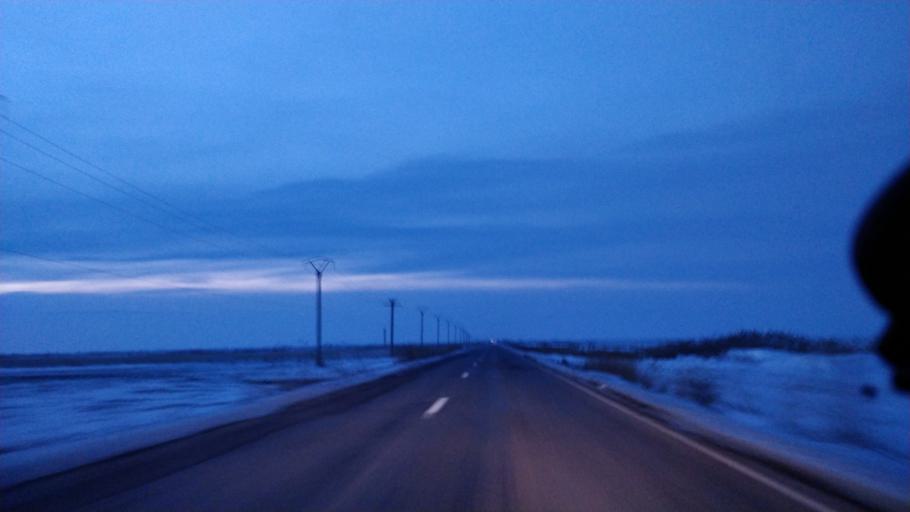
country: RO
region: Vrancea
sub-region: Comuna Vulturu
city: Vadu Rosca
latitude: 45.5971
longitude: 27.4654
